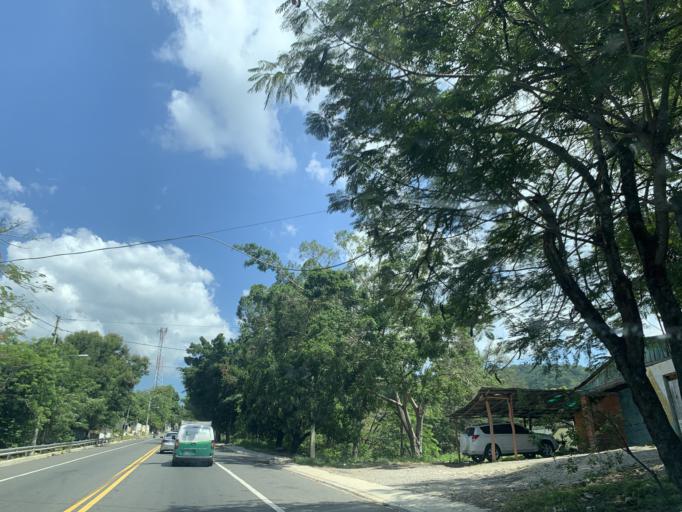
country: DO
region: Puerto Plata
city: Altamira
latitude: 19.6796
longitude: -70.8368
